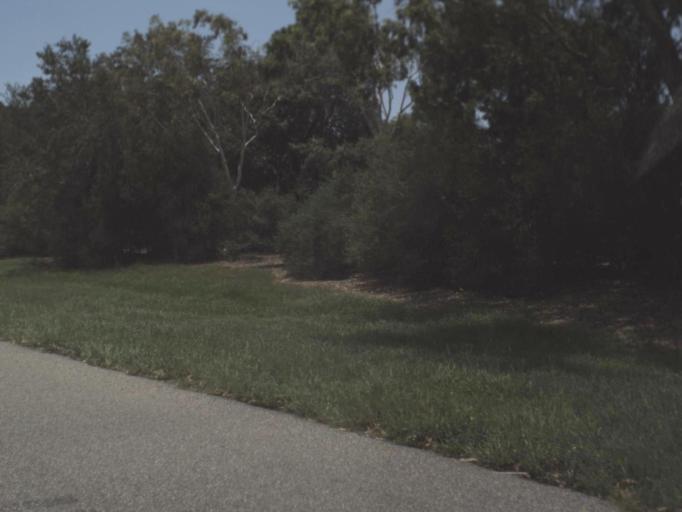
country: US
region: Florida
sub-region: Pinellas County
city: Lealman
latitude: 27.8386
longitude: -82.6638
